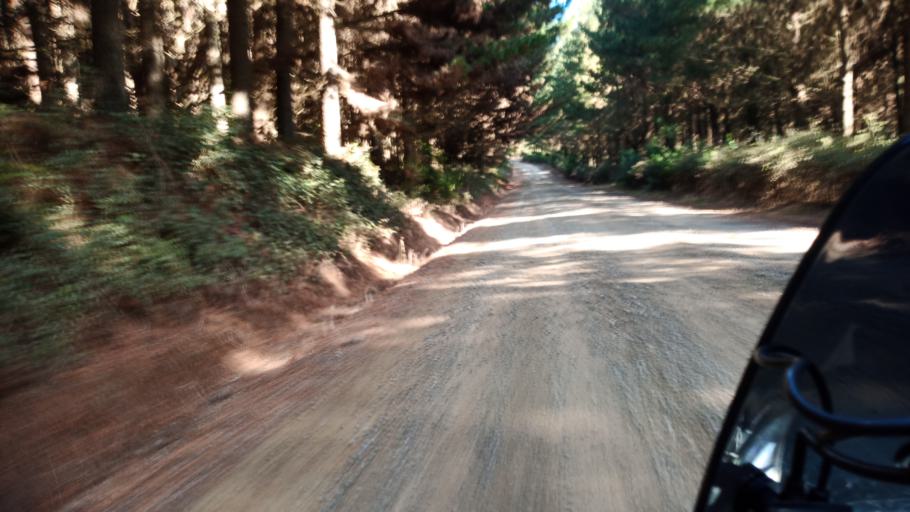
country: NZ
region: Hawke's Bay
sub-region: Wairoa District
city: Wairoa
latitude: -38.9321
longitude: 177.2318
